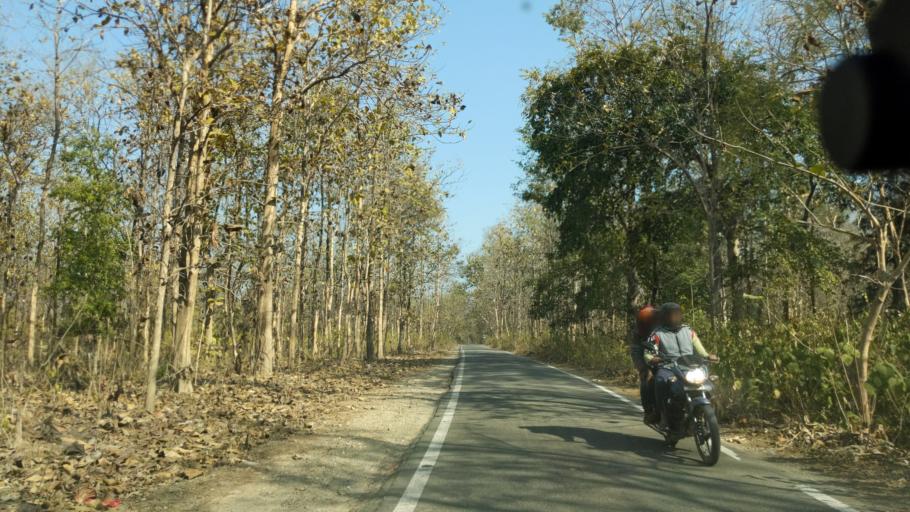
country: IN
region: Uttarakhand
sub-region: Naini Tal
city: Ramnagar
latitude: 29.4275
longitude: 79.1400
